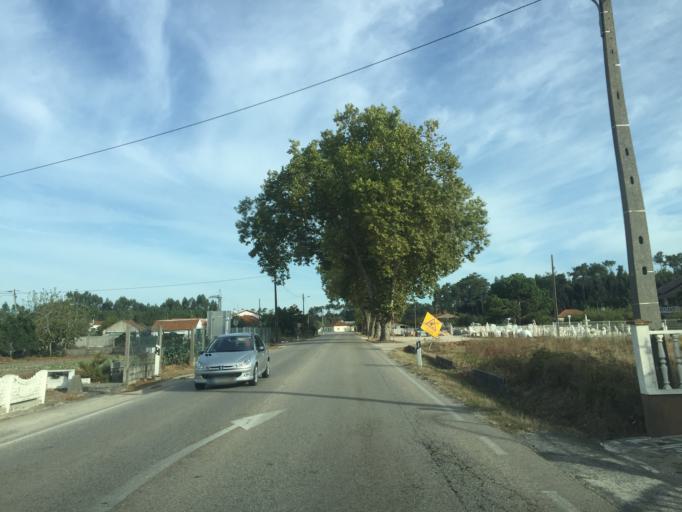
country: PT
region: Leiria
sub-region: Pombal
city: Lourical
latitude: 39.9563
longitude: -8.7864
